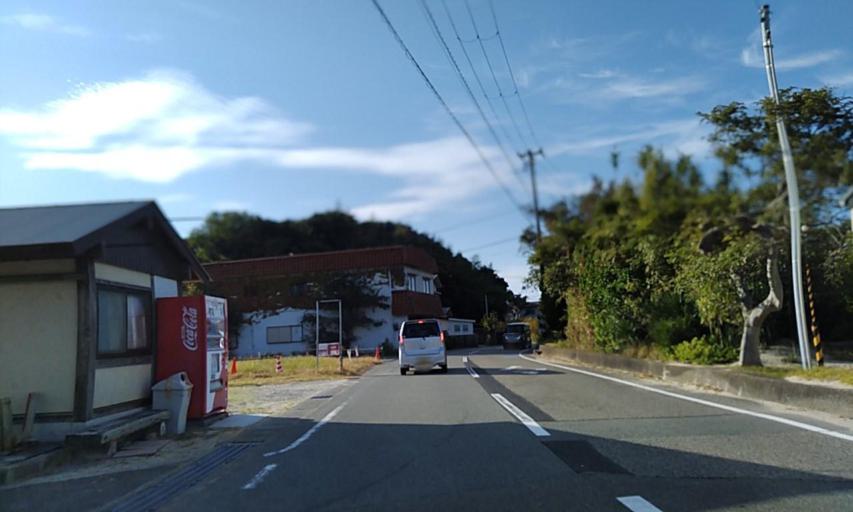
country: JP
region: Wakayama
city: Tanabe
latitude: 33.6930
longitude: 135.3504
